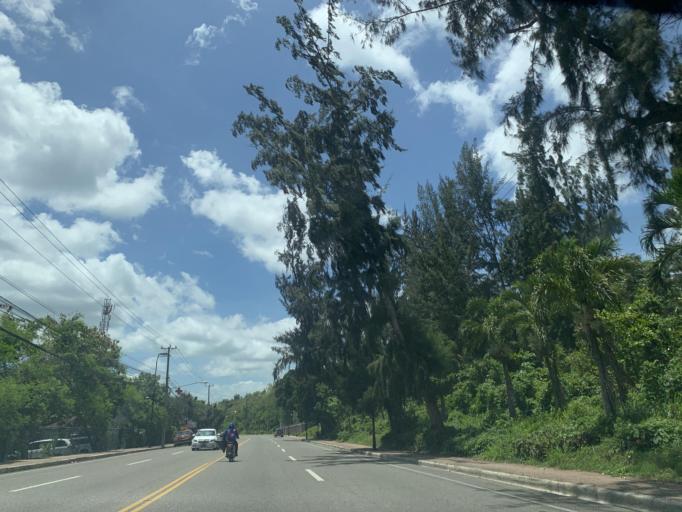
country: DO
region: Puerto Plata
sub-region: Puerto Plata
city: Puerto Plata
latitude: 19.7748
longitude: -70.6585
